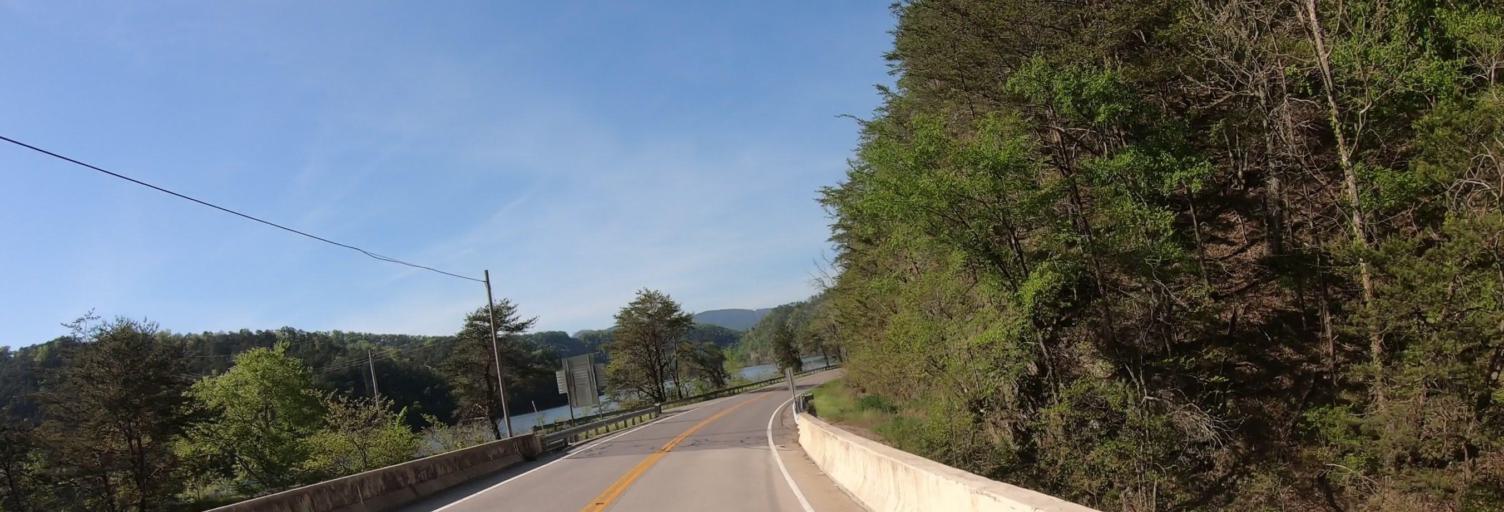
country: US
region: Tennessee
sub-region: Loudon County
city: Greenback
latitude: 35.5248
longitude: -83.9934
